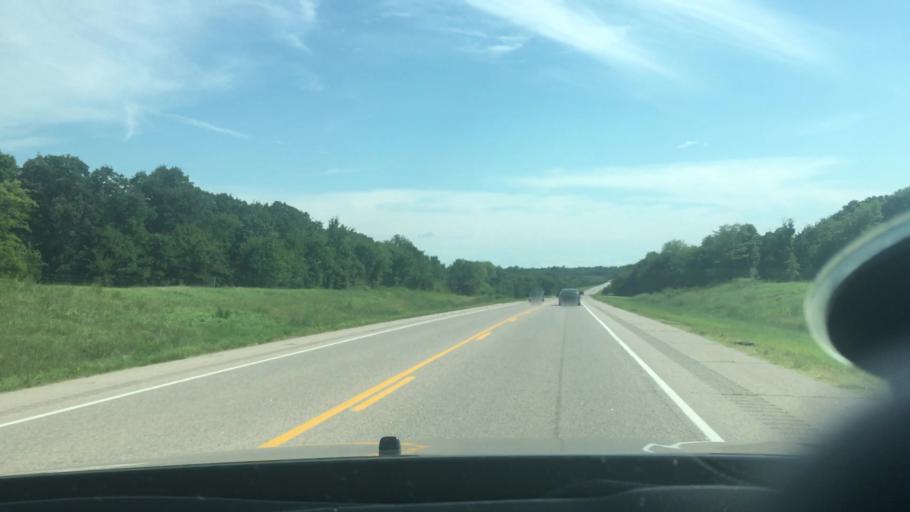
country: US
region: Oklahoma
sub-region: Seminole County
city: Maud
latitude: 35.0673
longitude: -96.6790
